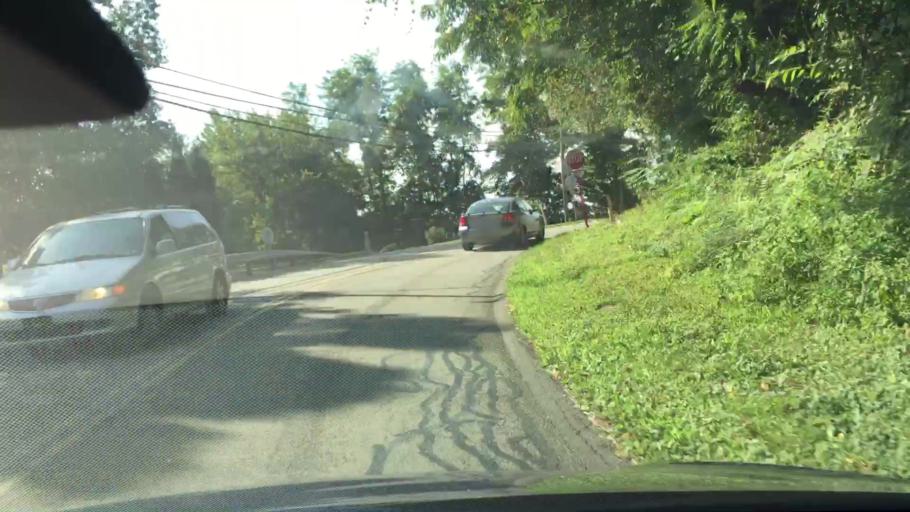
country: US
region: Pennsylvania
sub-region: Allegheny County
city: Pitcairn
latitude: 40.4231
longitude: -79.7615
